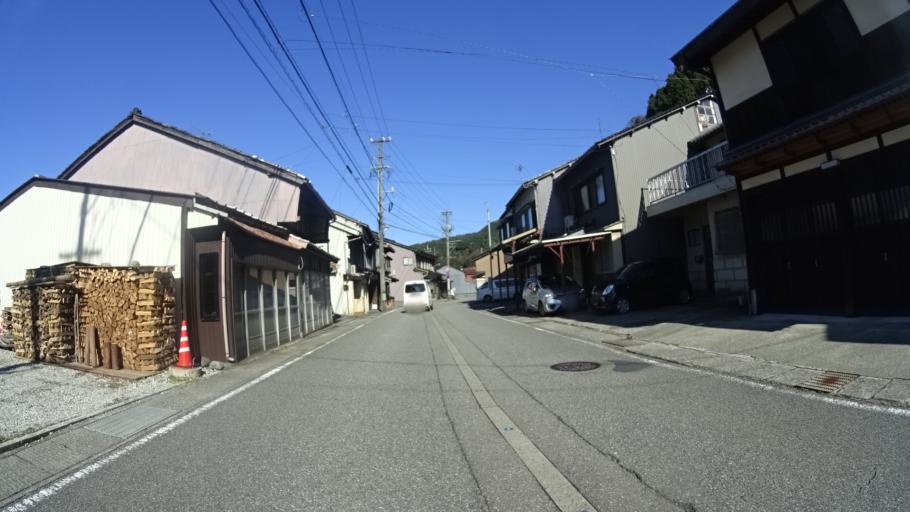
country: JP
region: Ishikawa
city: Tsurugi-asahimachi
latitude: 36.4429
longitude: 136.6305
